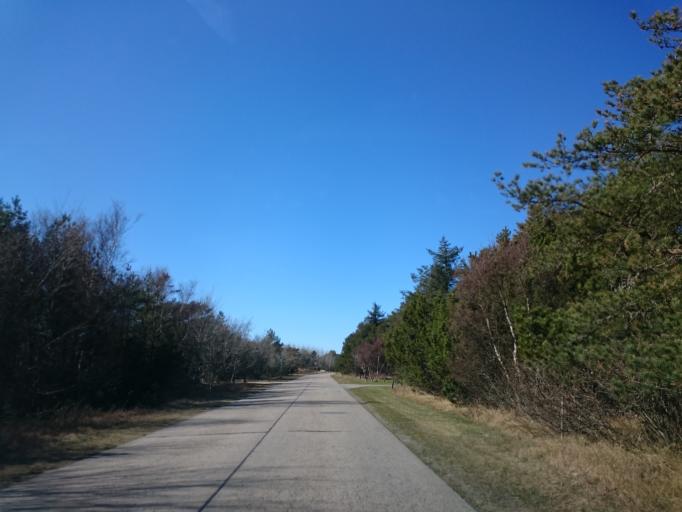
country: DK
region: North Denmark
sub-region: Frederikshavn Kommune
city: Skagen
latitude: 57.7203
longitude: 10.5356
